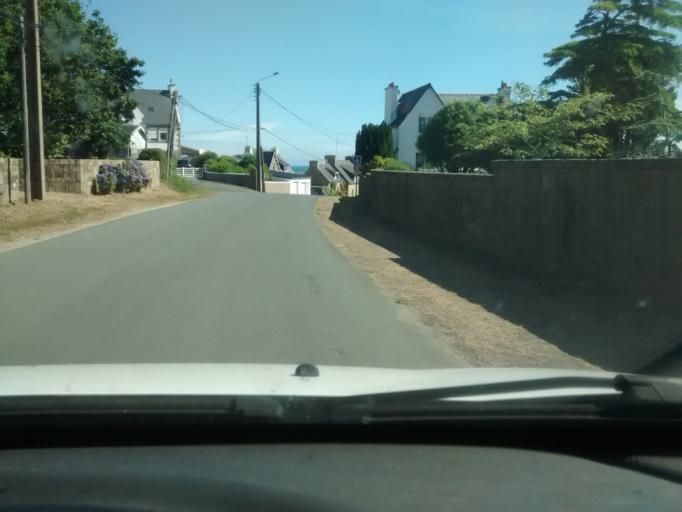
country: FR
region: Brittany
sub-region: Departement des Cotes-d'Armor
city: Trevou-Treguignec
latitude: 48.8239
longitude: -3.3428
